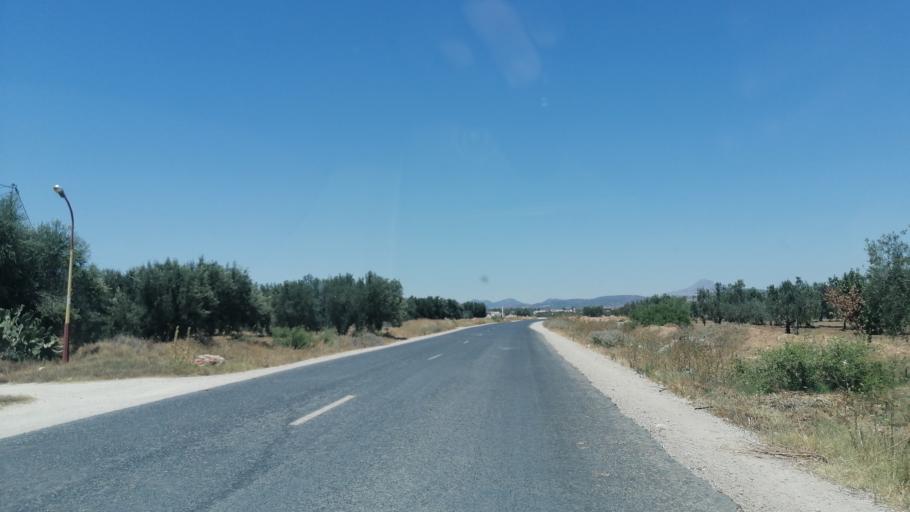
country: TN
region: Al Qayrawan
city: Sbikha
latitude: 36.1322
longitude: 10.0916
